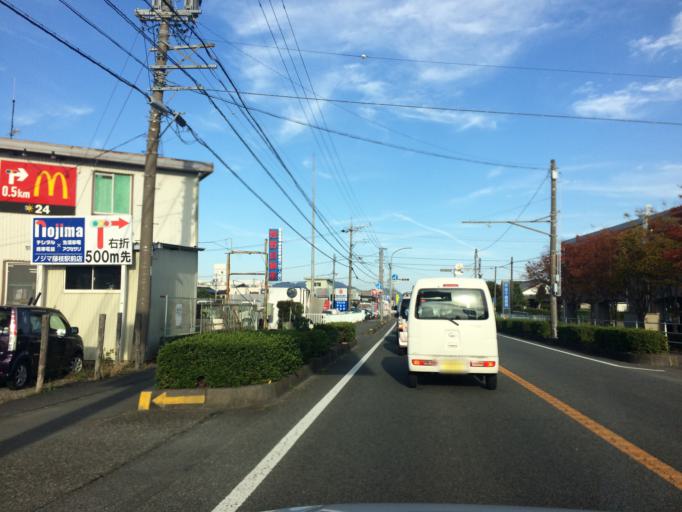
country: JP
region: Shizuoka
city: Fujieda
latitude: 34.8517
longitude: 138.2413
